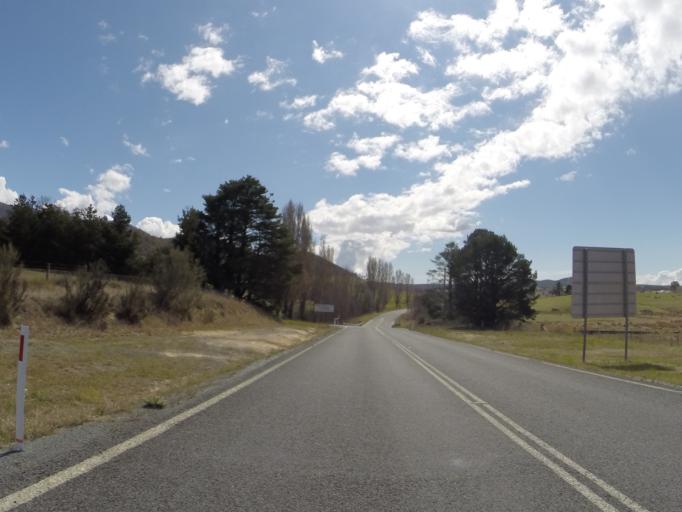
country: AU
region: Australian Capital Territory
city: Macarthur
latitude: -35.4158
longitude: 148.9464
